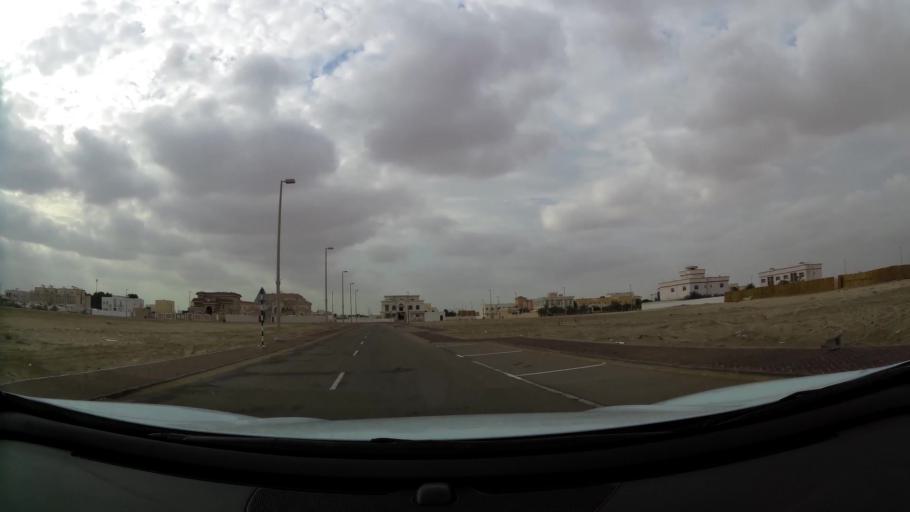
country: AE
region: Abu Dhabi
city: Abu Dhabi
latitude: 24.3466
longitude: 54.6212
